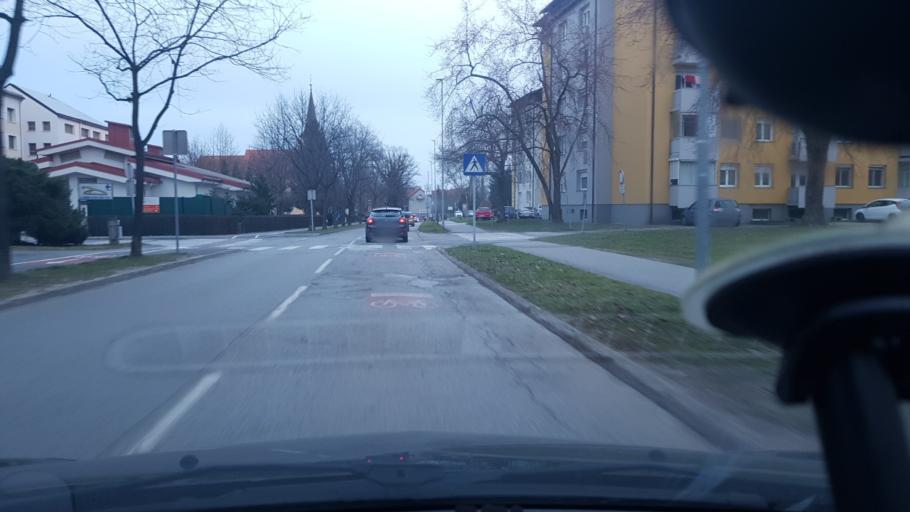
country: SI
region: Ptuj
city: Ptuj
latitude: 46.4248
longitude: 15.8729
